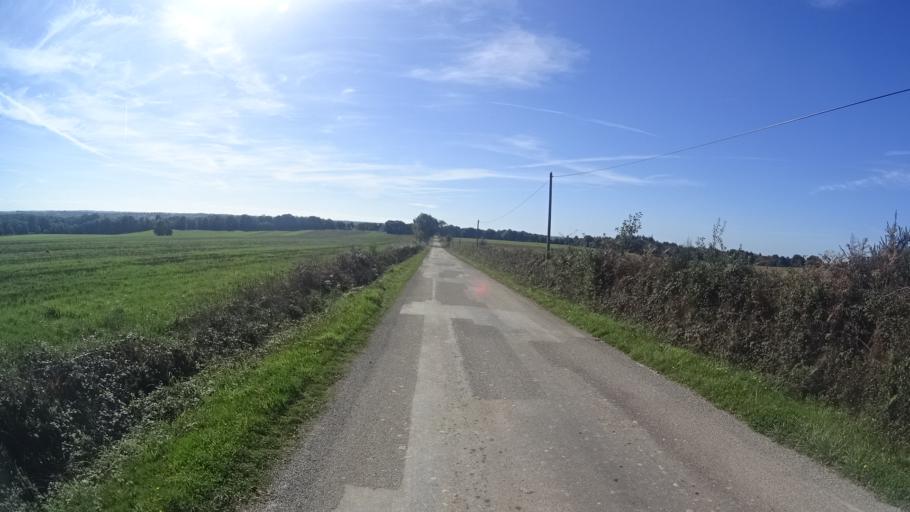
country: FR
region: Brittany
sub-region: Departement du Morbihan
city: La Gacilly
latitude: 47.7456
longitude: -2.1715
